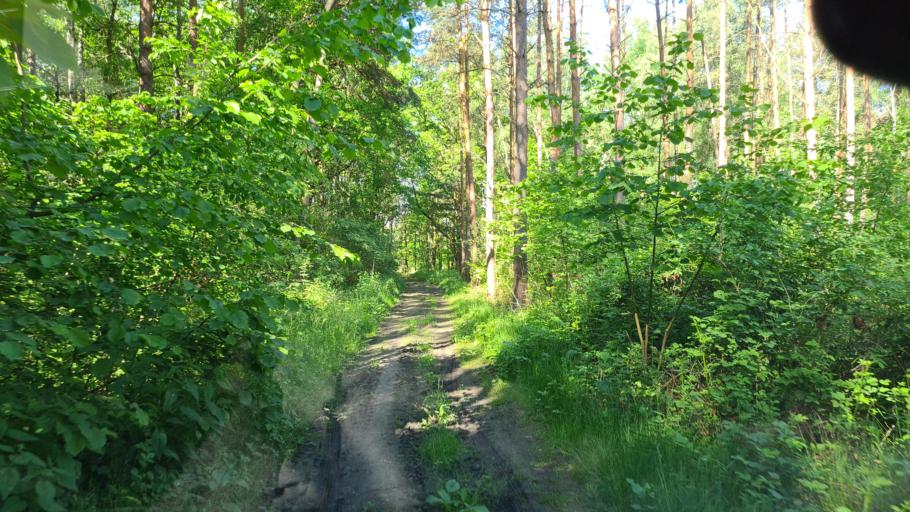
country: DE
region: Brandenburg
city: Ruckersdorf
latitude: 51.6027
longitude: 13.6034
